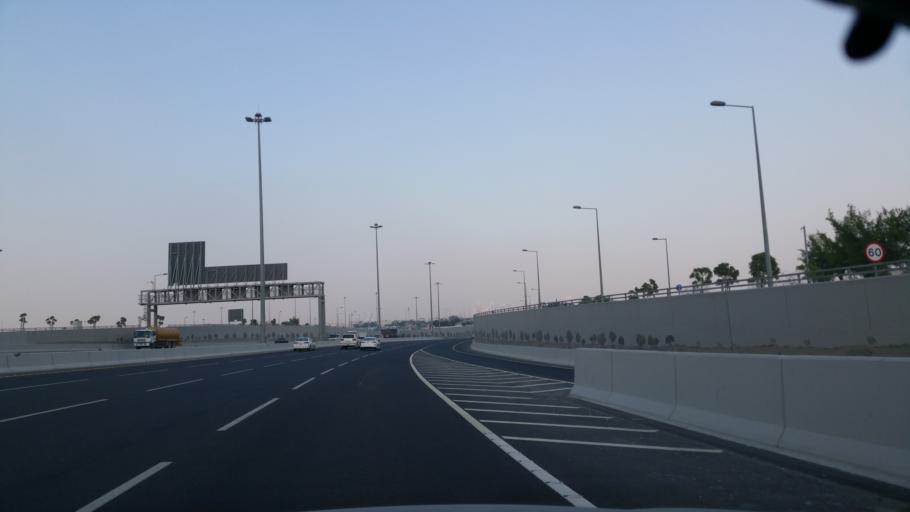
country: QA
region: Baladiyat ar Rayyan
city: Ar Rayyan
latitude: 25.3008
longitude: 51.4500
